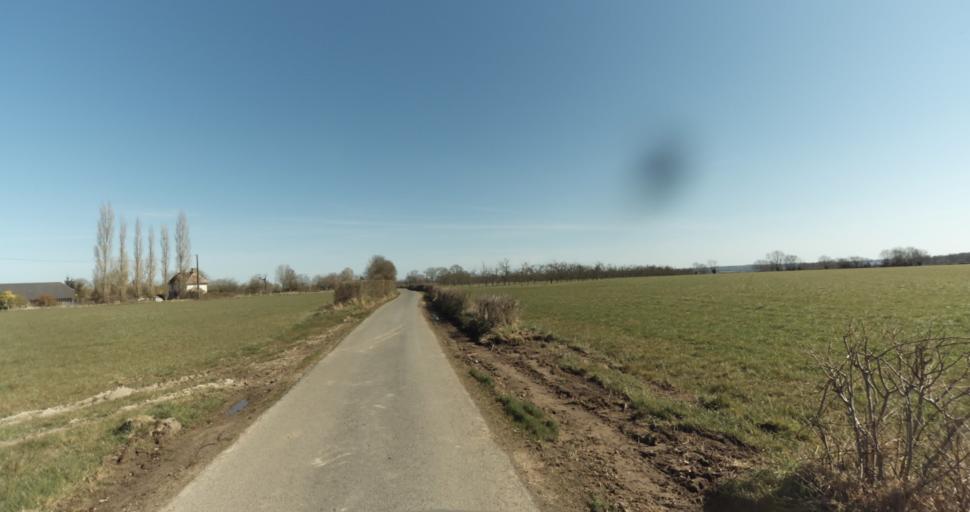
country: FR
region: Lower Normandy
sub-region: Departement du Calvados
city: Livarot
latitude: 48.9830
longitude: 0.1044
